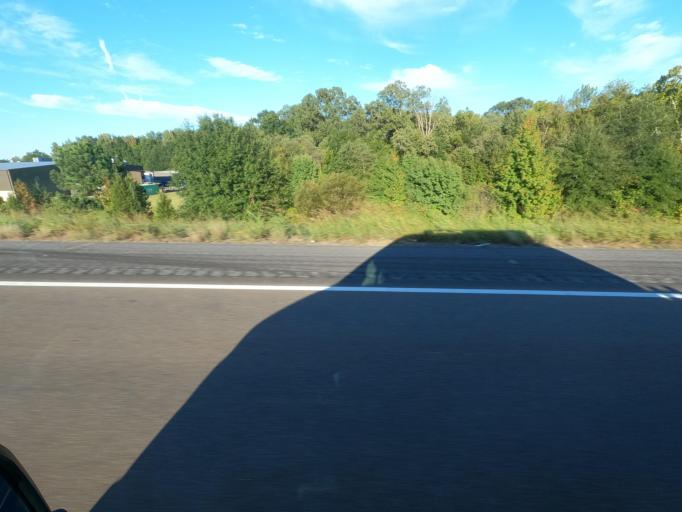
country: US
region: Tennessee
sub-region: Shelby County
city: Arlington
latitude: 35.2852
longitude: -89.6826
